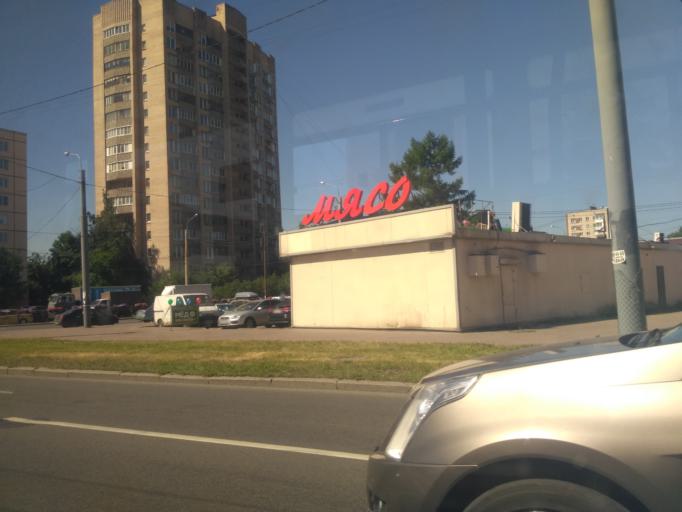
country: RU
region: Leningrad
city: Kalininskiy
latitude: 59.9690
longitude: 30.4108
